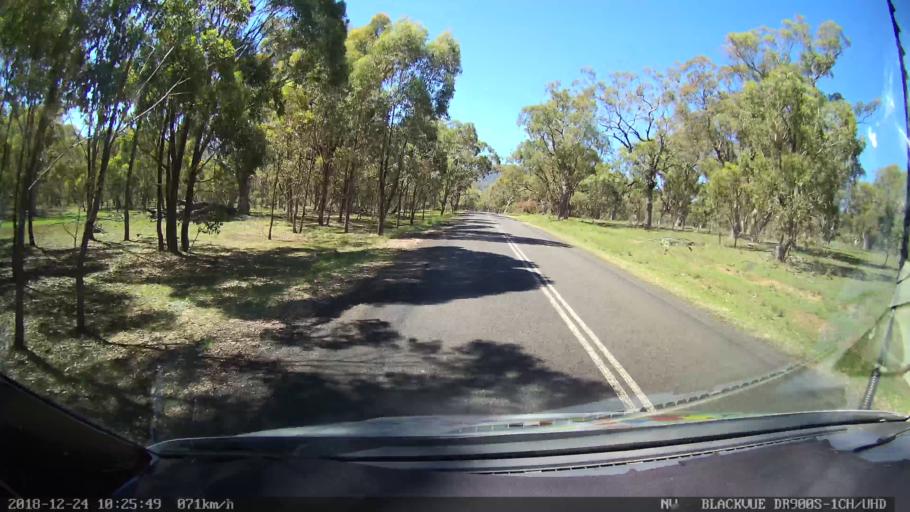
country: AU
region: New South Wales
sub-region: Liverpool Plains
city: Quirindi
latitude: -31.8030
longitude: 150.5274
